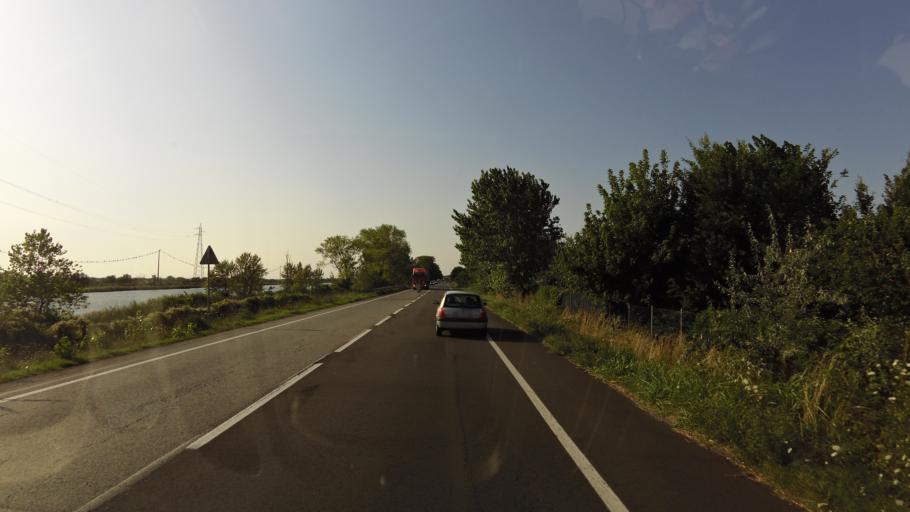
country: IT
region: Emilia-Romagna
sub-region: Provincia di Ravenna
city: Cervia
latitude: 44.2439
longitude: 12.3516
